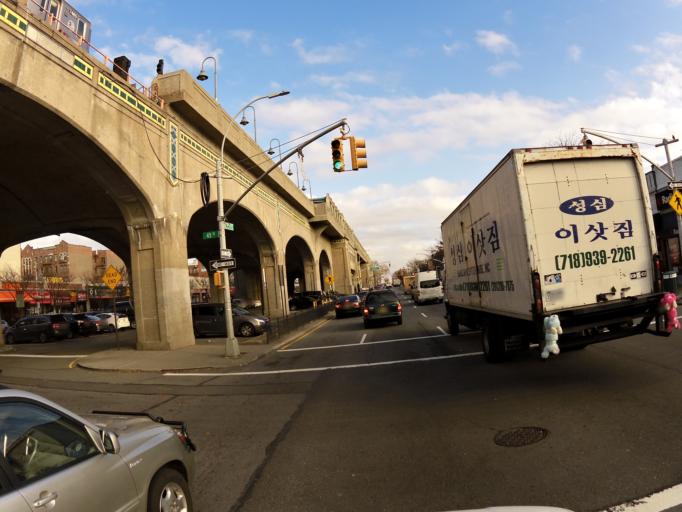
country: US
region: New York
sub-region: Queens County
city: Long Island City
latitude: 40.7432
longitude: -73.9197
